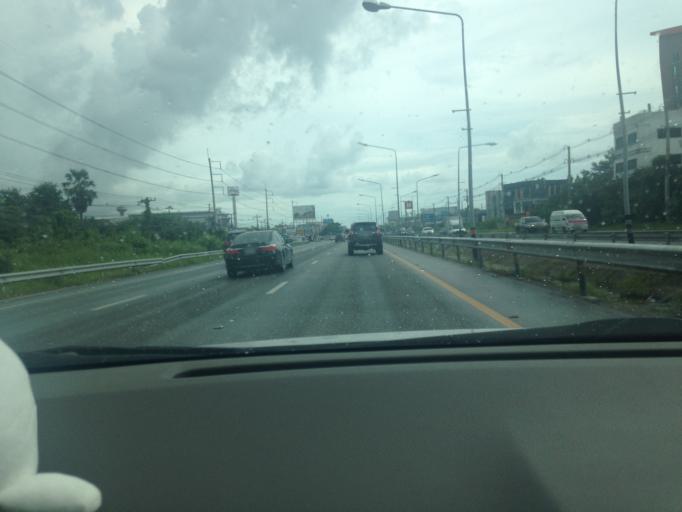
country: TH
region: Chon Buri
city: Chon Buri
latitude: 13.3033
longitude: 100.9502
